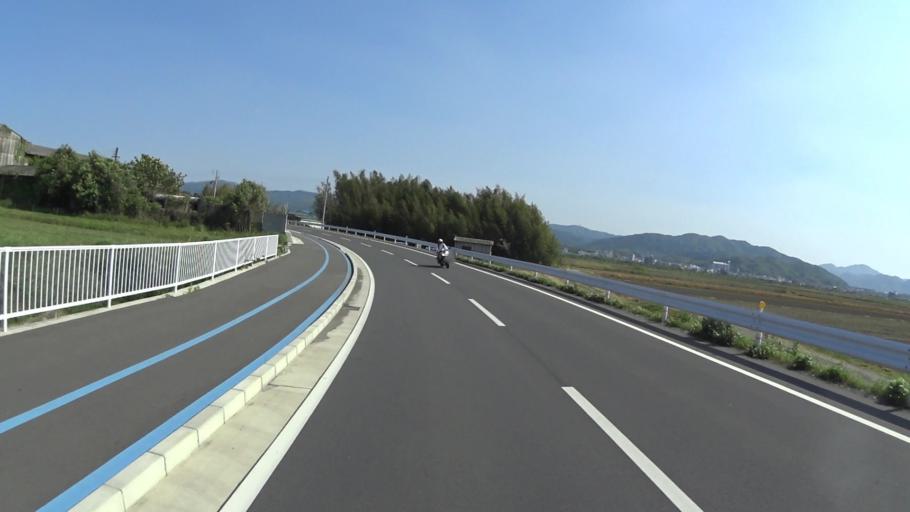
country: JP
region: Kyoto
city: Kameoka
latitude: 35.0335
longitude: 135.5829
